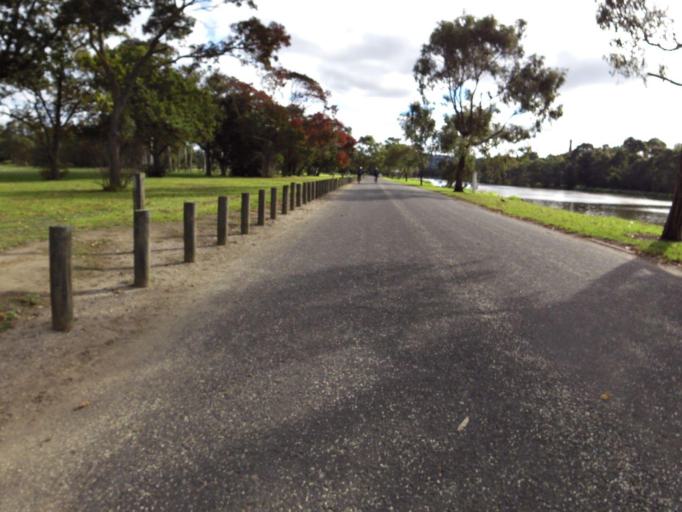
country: AU
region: Victoria
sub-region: Greater Geelong
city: Geelong
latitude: -38.1643
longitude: 144.3421
